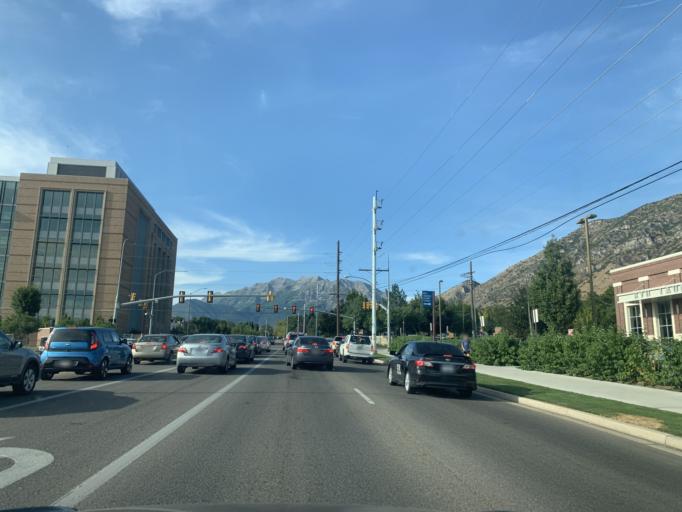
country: US
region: Utah
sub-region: Utah County
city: Provo
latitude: 40.2560
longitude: -111.6432
